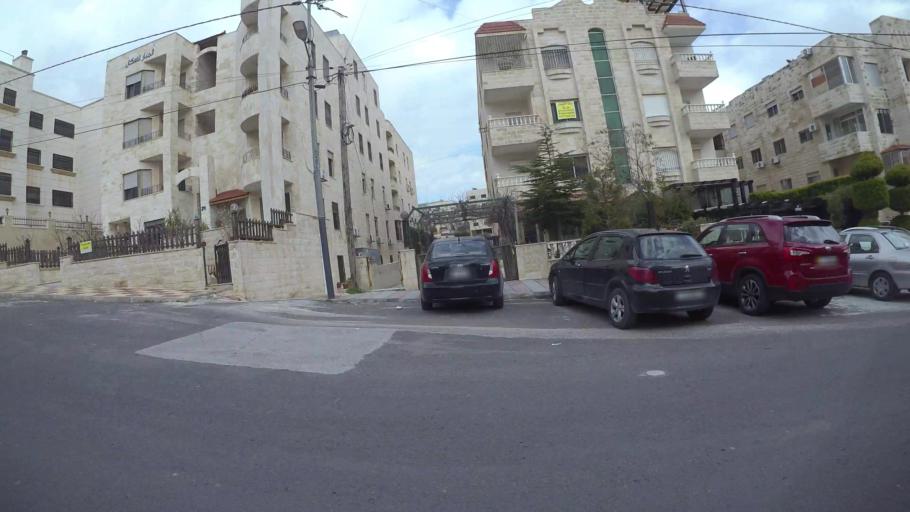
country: JO
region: Amman
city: Wadi as Sir
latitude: 31.9843
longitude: 35.8423
